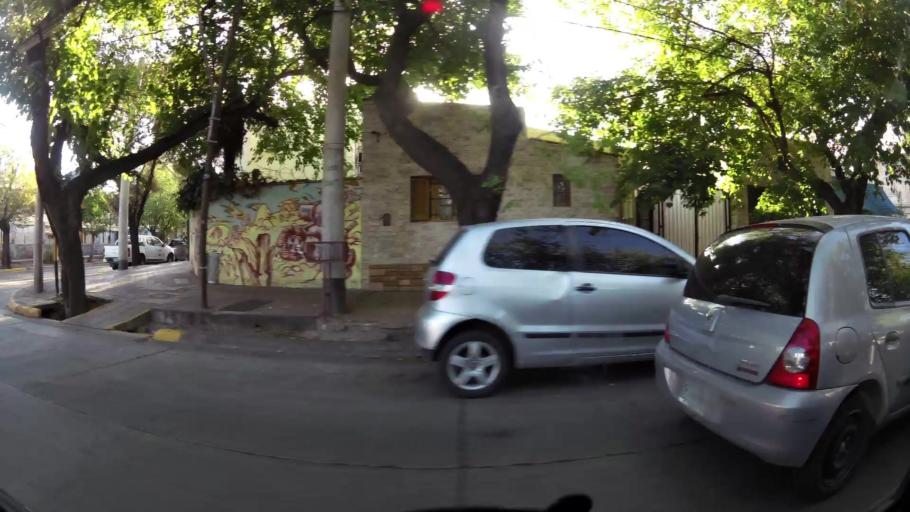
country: AR
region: Mendoza
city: Mendoza
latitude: -32.9013
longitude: -68.8409
